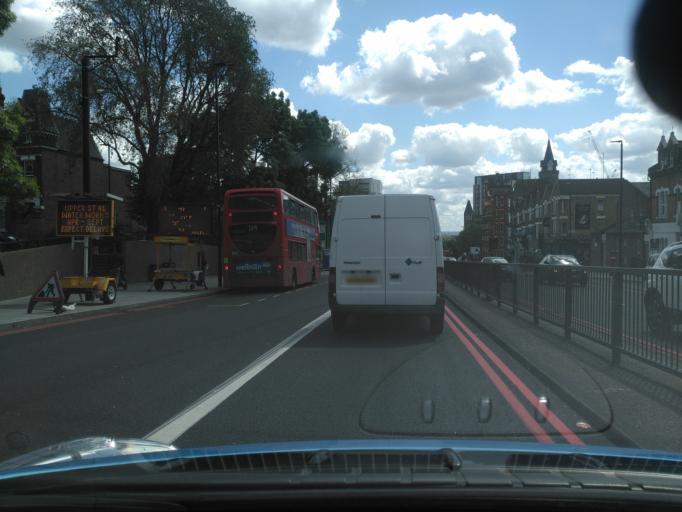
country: GB
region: England
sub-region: Greater London
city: Crouch End
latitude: 51.5691
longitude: -0.1369
